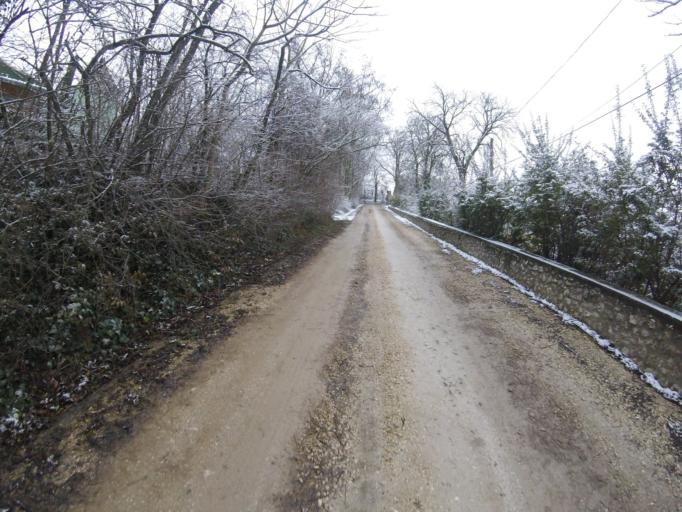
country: HU
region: Komarom-Esztergom
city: Esztergom
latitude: 47.7876
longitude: 18.7493
